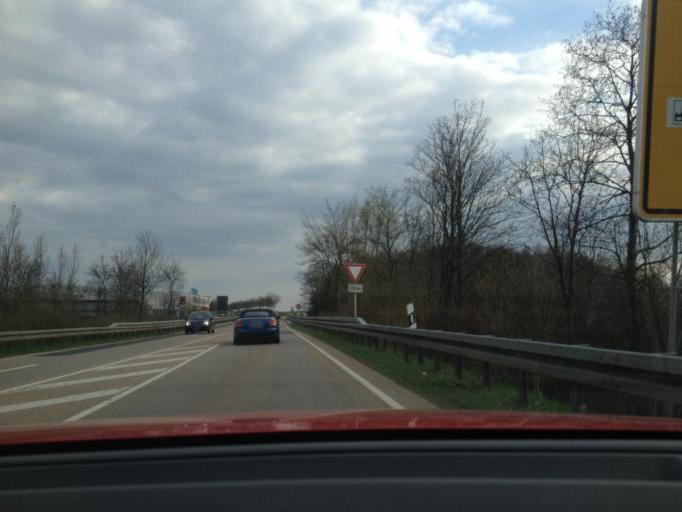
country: DE
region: Bavaria
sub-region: Upper Palatinate
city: Kemnath
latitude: 49.8672
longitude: 11.8757
